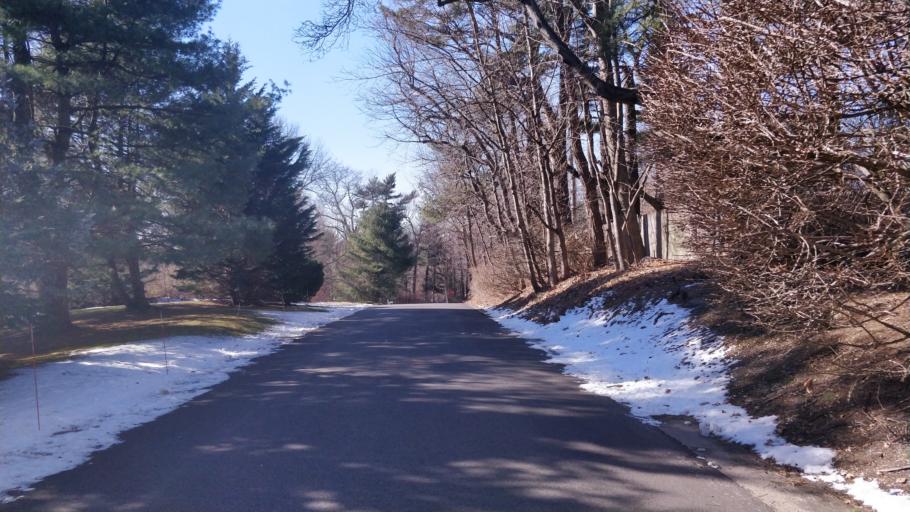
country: US
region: New York
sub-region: Nassau County
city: Westbury
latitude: 40.7753
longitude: -73.5844
